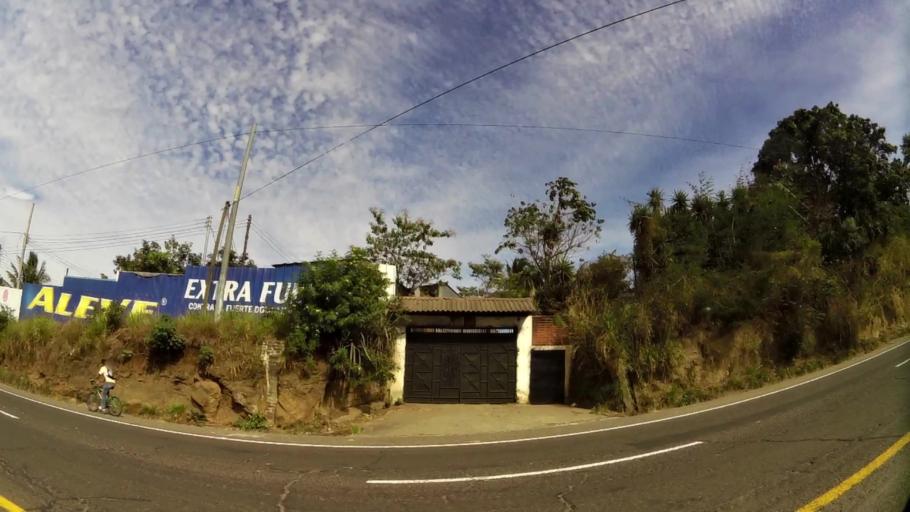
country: SV
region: Santa Ana
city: Chalchuapa
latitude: 13.9837
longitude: -89.6906
